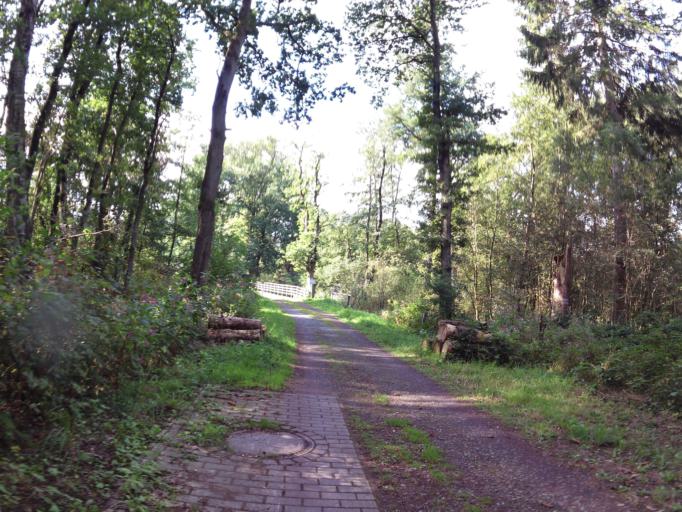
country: DE
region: Lower Saxony
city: Bremervorde
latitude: 53.4706
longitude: 9.1445
